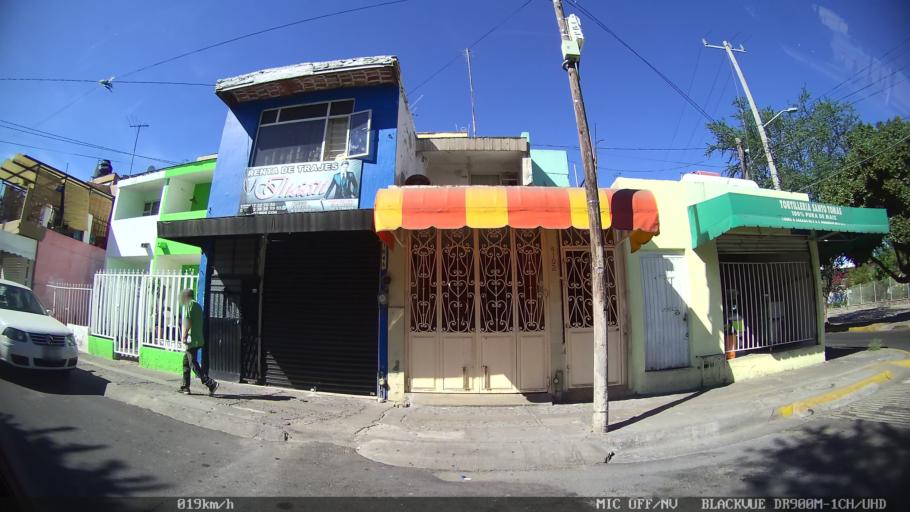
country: MX
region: Jalisco
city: Tlaquepaque
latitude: 20.6811
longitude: -103.2726
